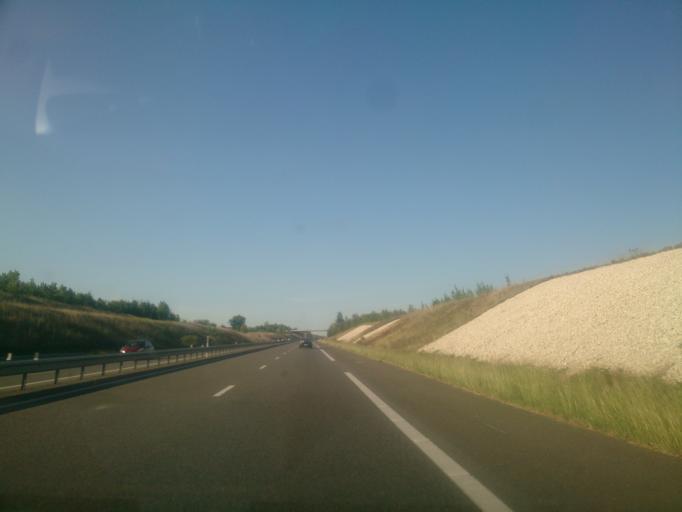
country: FR
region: Midi-Pyrenees
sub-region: Departement du Tarn-et-Garonne
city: Caussade
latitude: 44.1868
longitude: 1.5351
